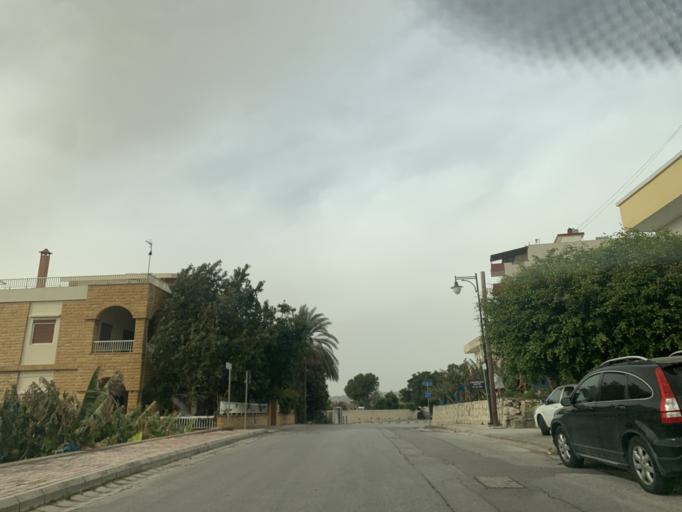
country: LB
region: Mont-Liban
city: Jbail
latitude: 34.0928
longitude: 35.6510
